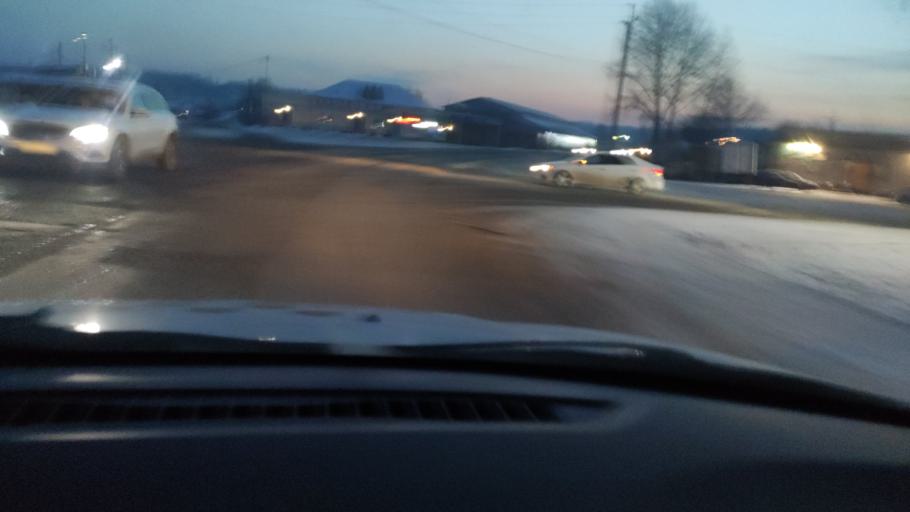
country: RU
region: Perm
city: Kungur
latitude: 57.4257
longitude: 56.9317
